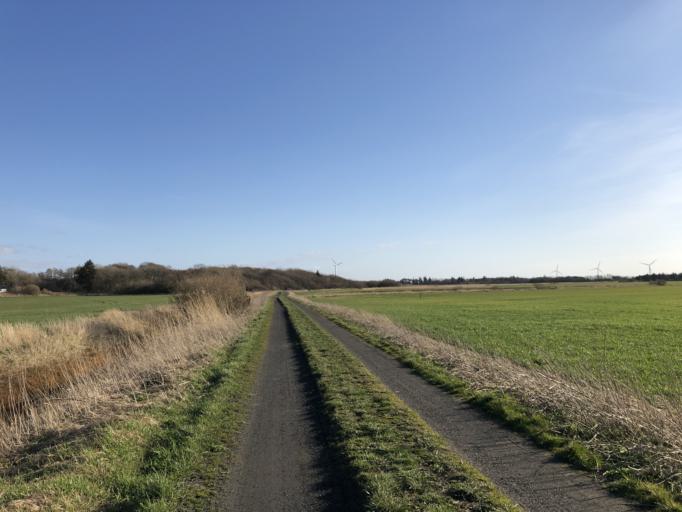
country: DK
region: Central Jutland
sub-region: Holstebro Kommune
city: Ulfborg
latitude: 56.3309
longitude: 8.3267
